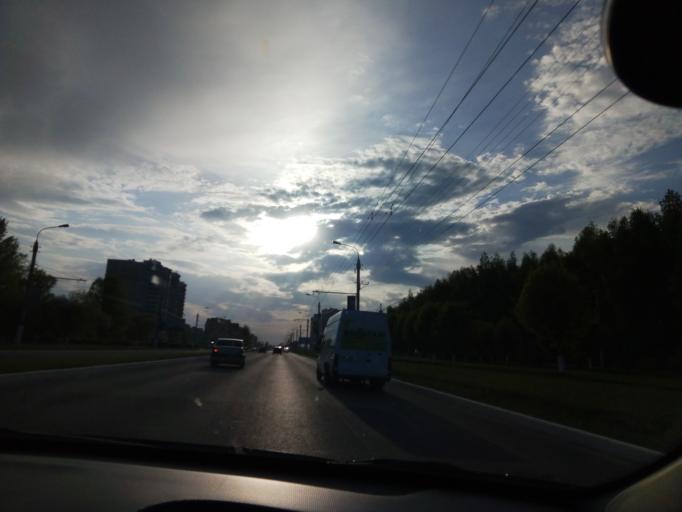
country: RU
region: Chuvashia
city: Novocheboksarsk
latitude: 56.1186
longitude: 47.4710
